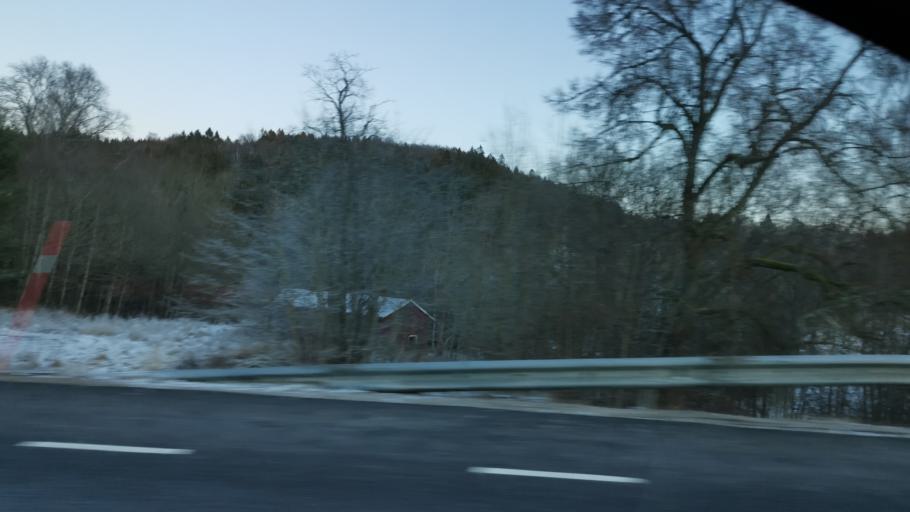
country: SE
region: Vaestra Goetaland
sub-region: Munkedals Kommun
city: Munkedal
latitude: 58.4290
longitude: 11.7224
